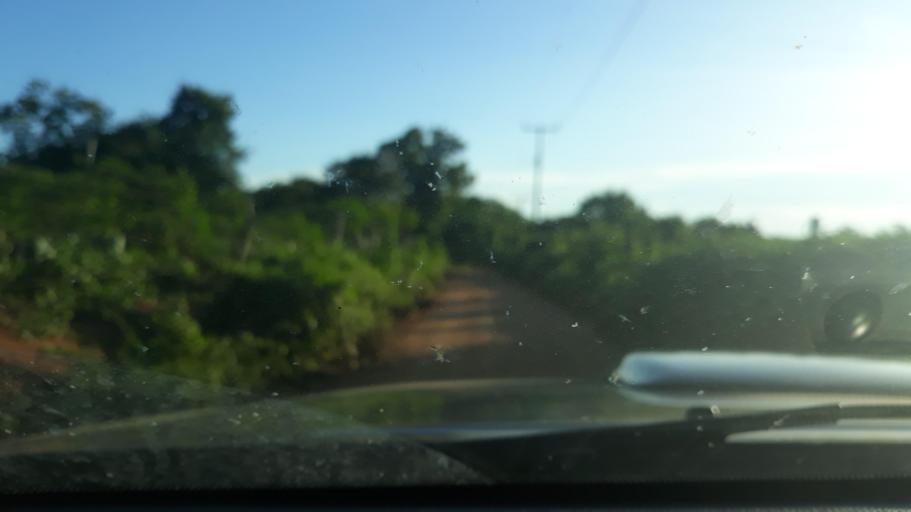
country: BR
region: Bahia
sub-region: Riacho De Santana
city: Riacho de Santana
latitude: -13.8419
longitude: -42.7376
